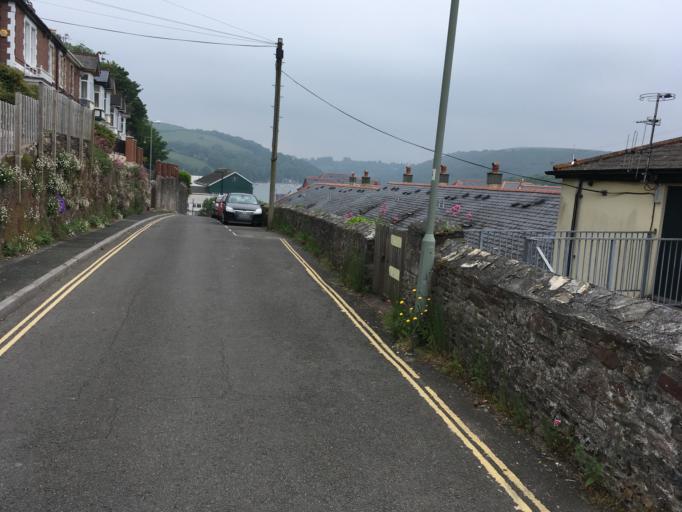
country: GB
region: England
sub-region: Devon
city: Dartmouth
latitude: 50.3575
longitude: -3.5778
